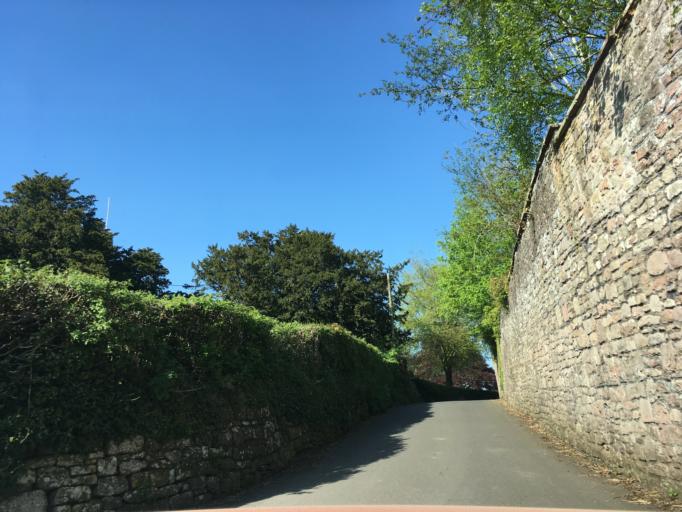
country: GB
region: Wales
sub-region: Monmouthshire
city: Caldicot
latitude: 51.6378
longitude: -2.7549
